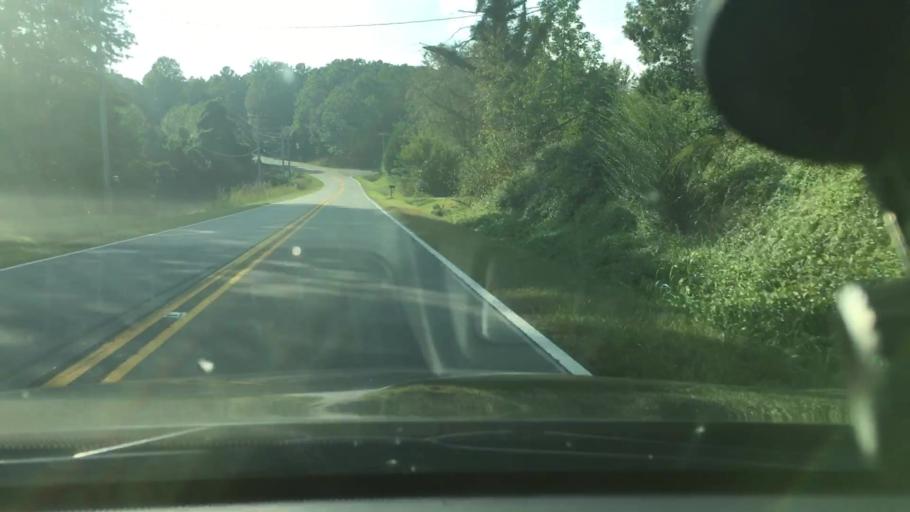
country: US
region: North Carolina
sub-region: Polk County
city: Columbus
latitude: 35.3151
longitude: -82.1383
